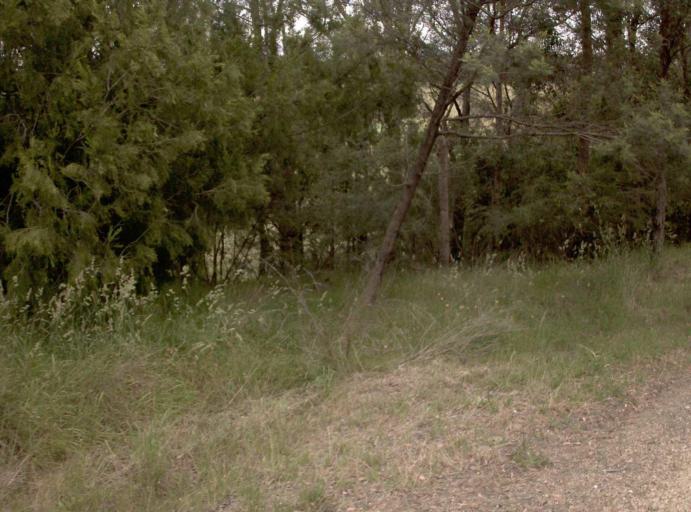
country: AU
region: Victoria
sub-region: East Gippsland
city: Bairnsdale
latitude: -37.7781
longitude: 147.5979
